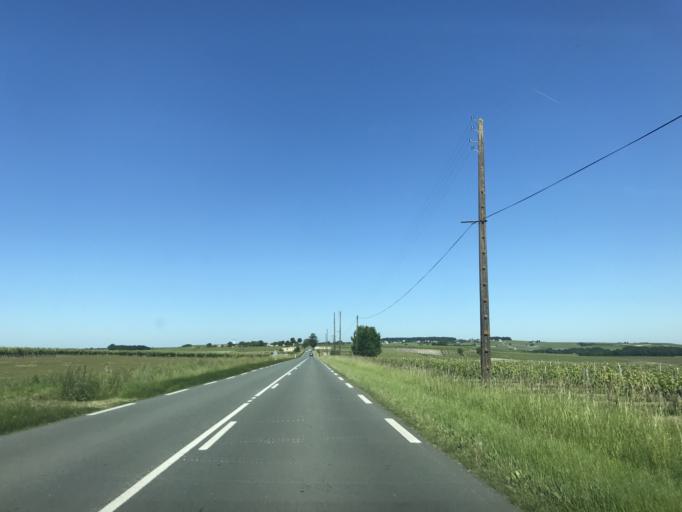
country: FR
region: Poitou-Charentes
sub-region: Departement de la Charente-Maritime
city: Perignac
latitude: 45.5739
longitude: -0.4239
